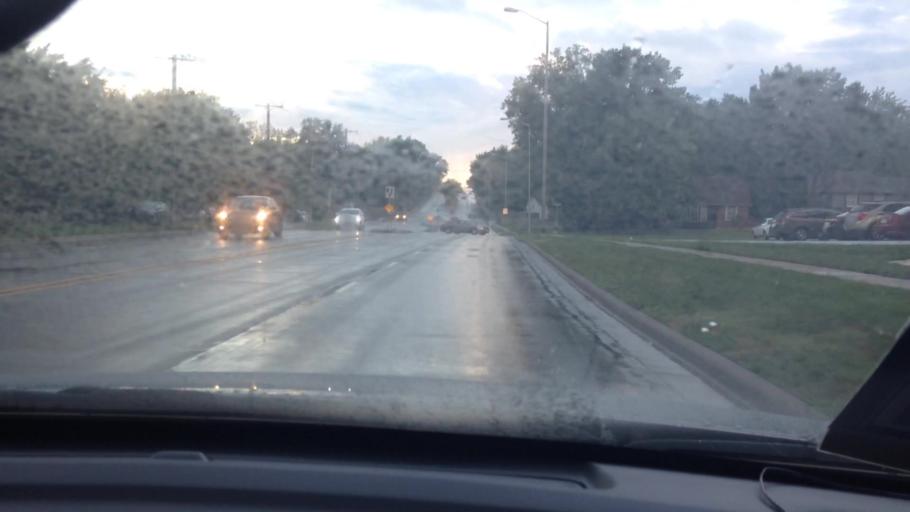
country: US
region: Kansas
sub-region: Johnson County
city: Lenexa
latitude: 38.9421
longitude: -94.6938
